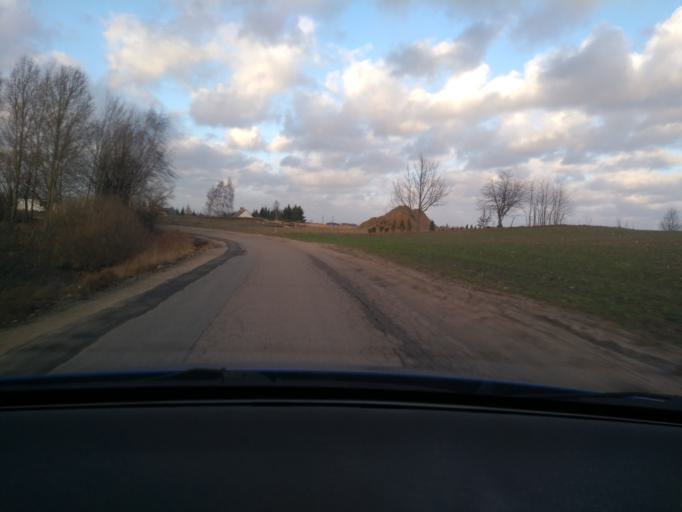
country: PL
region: Pomeranian Voivodeship
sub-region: Powiat kartuski
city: Przodkowo
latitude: 54.3954
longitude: 18.2254
